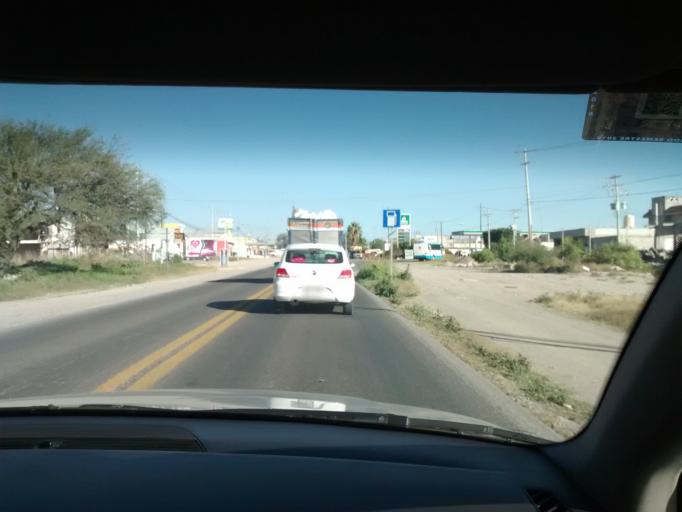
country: MX
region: Puebla
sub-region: Tehuacan
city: Magdalena Cuayucatepec
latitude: 18.5179
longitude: -97.5025
